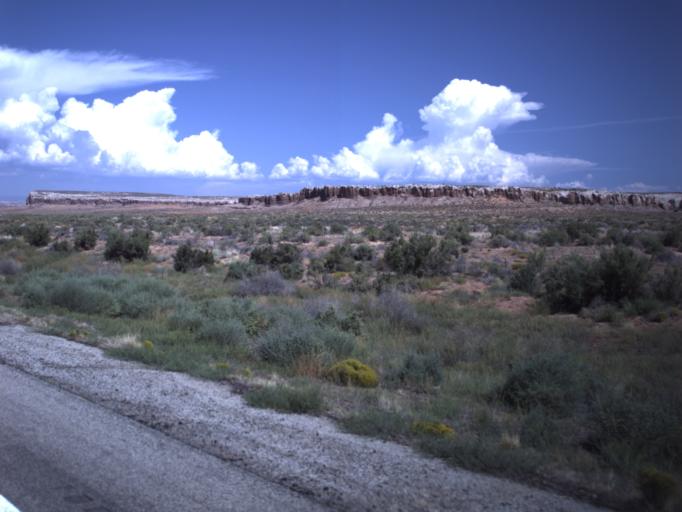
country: US
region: Utah
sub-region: San Juan County
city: Blanding
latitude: 37.1933
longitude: -109.5980
